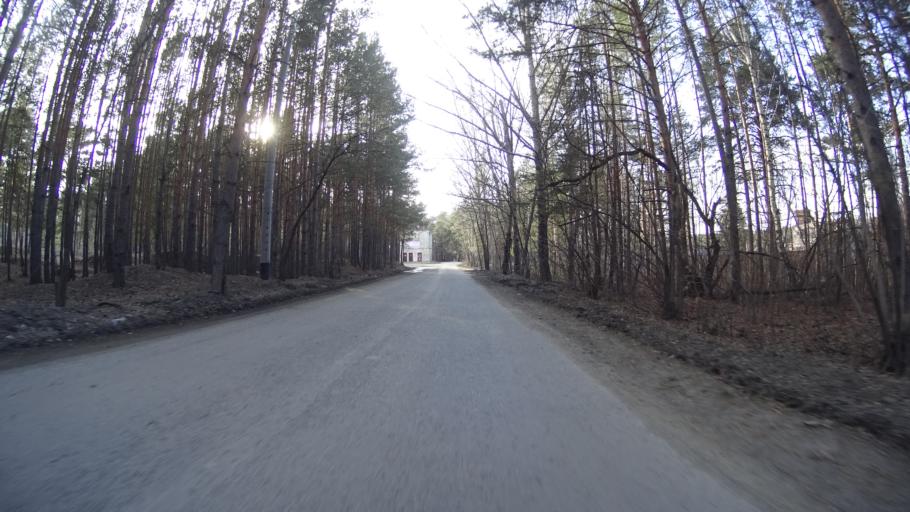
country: RU
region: Chelyabinsk
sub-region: Gorod Chelyabinsk
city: Chelyabinsk
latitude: 55.1282
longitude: 61.3593
